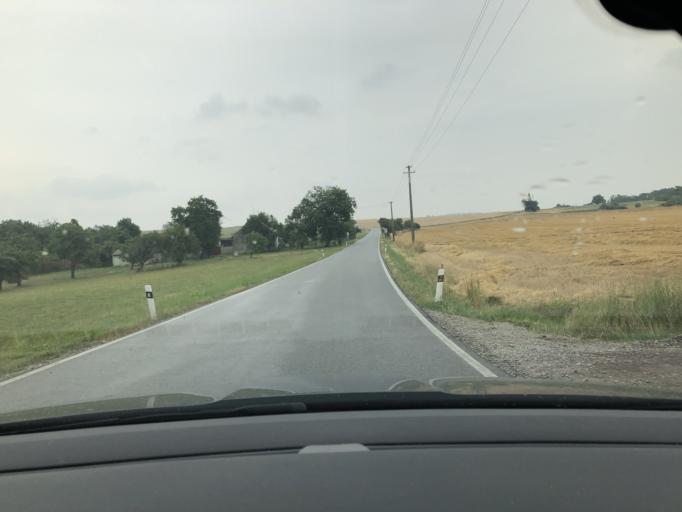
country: CZ
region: South Moravian
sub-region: Okres Znojmo
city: Jevisovice
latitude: 49.0287
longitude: 15.9934
